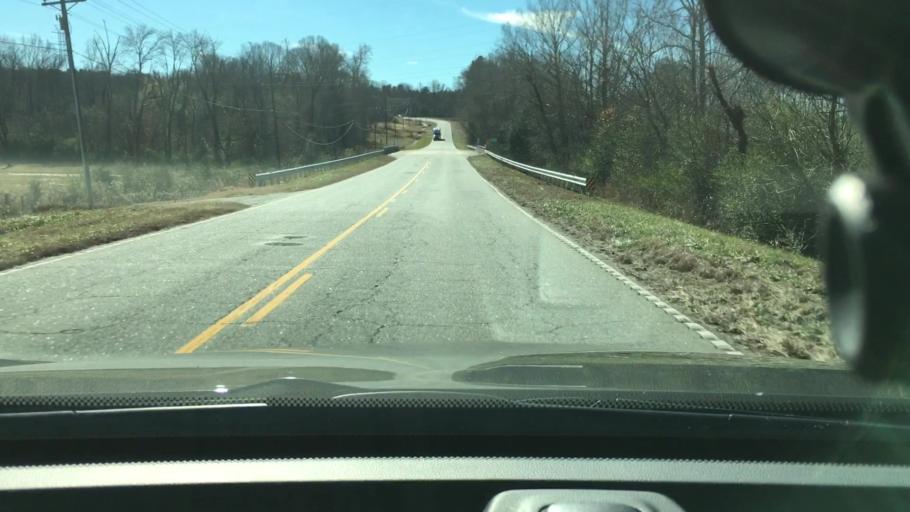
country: US
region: South Carolina
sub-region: Cherokee County
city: Gaffney
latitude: 35.0247
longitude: -81.6884
